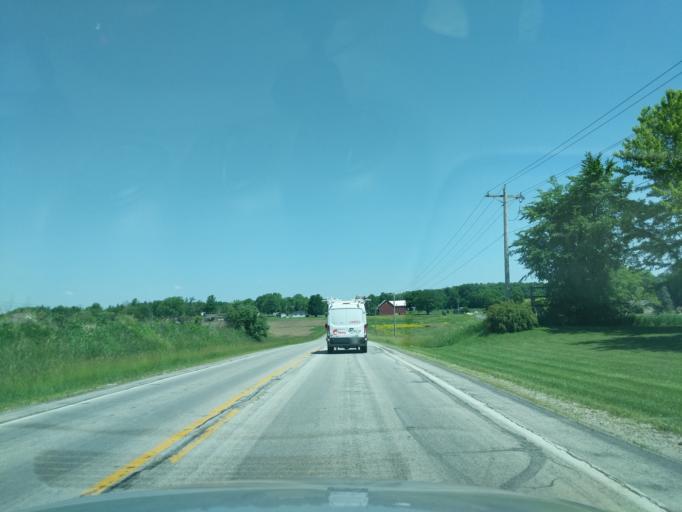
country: US
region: Indiana
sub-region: Whitley County
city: Columbia City
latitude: 41.1887
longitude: -85.4915
